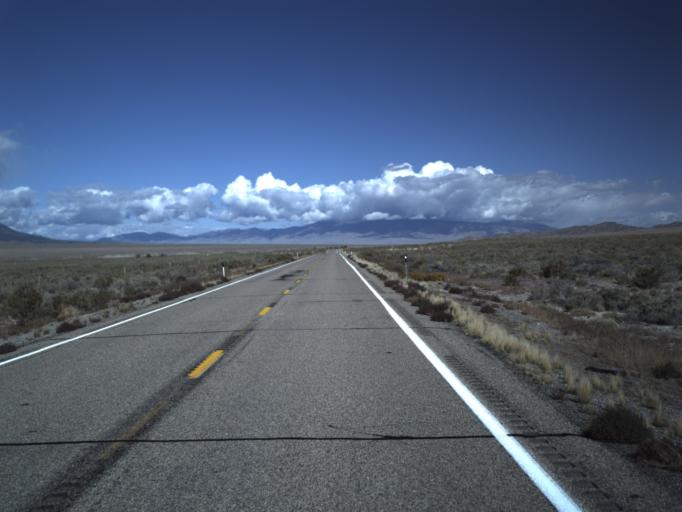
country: US
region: Nevada
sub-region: White Pine County
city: McGill
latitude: 38.8099
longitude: -113.9808
